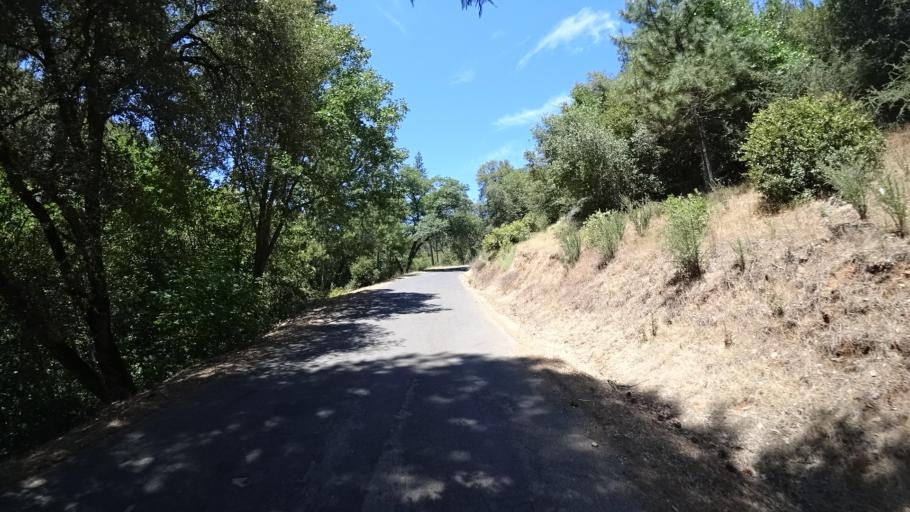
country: US
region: California
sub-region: Calaveras County
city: Forest Meadows
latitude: 38.2033
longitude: -120.4516
